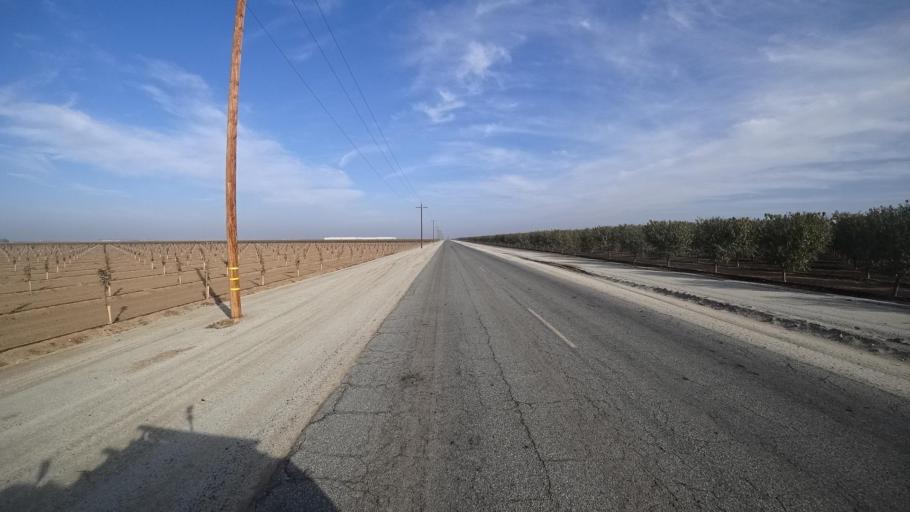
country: US
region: California
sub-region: Kern County
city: McFarland
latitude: 35.6937
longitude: -119.2049
